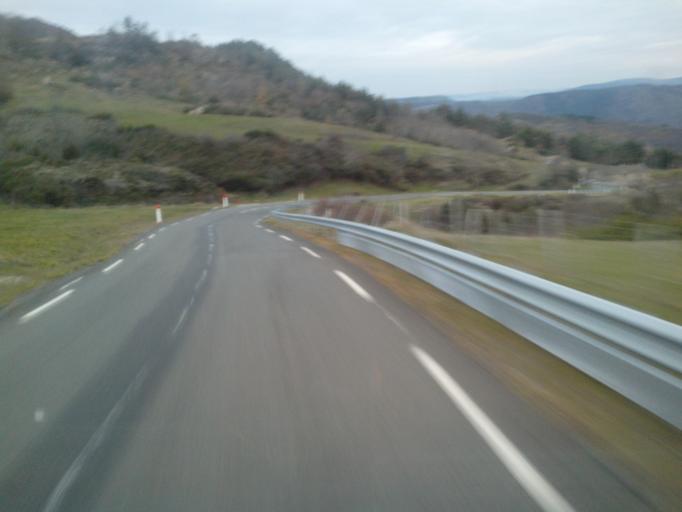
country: FR
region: Languedoc-Roussillon
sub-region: Departement du Gard
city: Valleraugue
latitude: 44.1923
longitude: 3.6471
